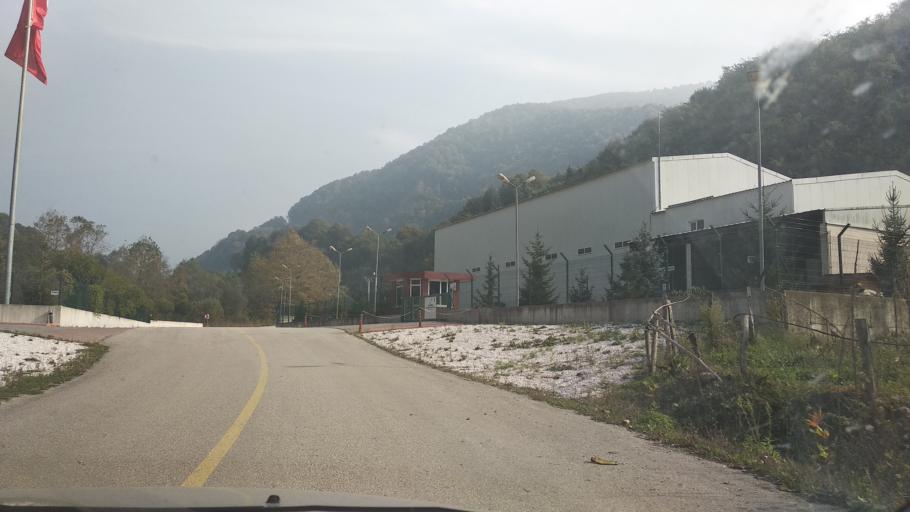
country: TR
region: Duzce
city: Duzce
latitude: 40.7364
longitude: 31.2083
